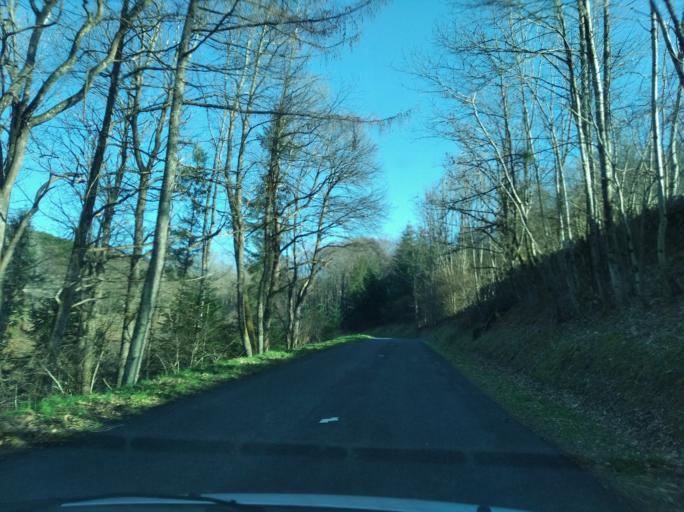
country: FR
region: Auvergne
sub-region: Departement de l'Allier
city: Le Mayet-de-Montagne
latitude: 46.1015
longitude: 3.7575
